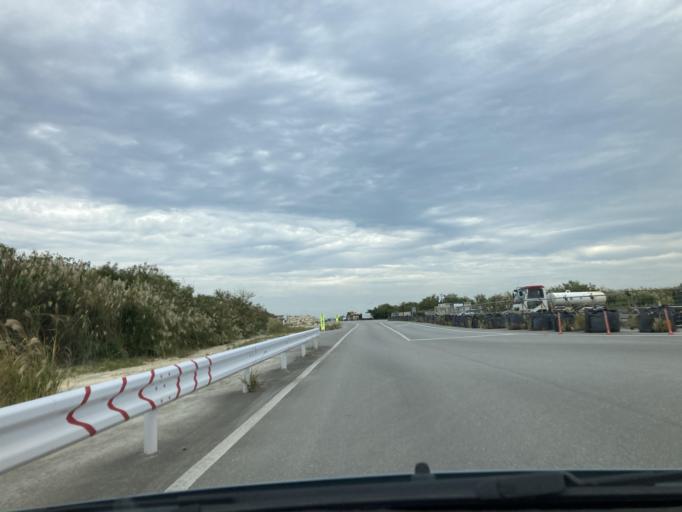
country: JP
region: Okinawa
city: Okinawa
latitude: 26.3868
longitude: 127.7460
